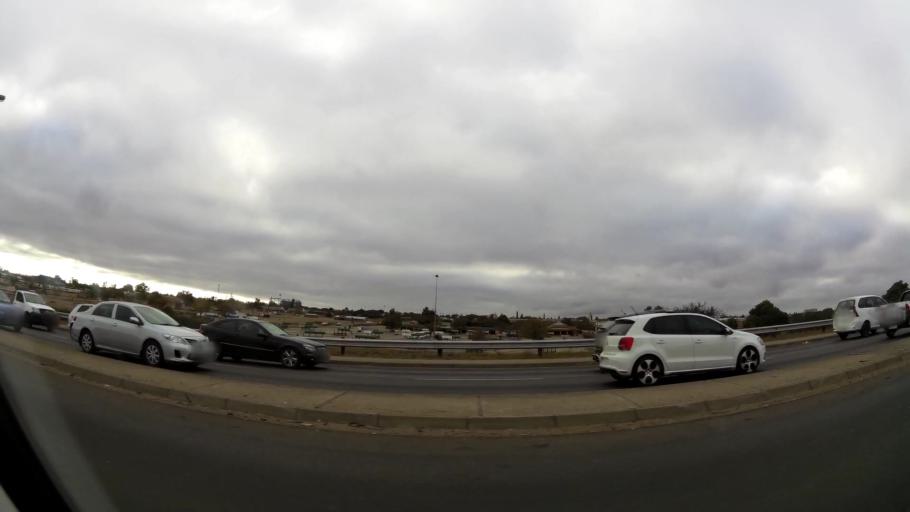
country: ZA
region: Limpopo
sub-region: Capricorn District Municipality
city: Polokwane
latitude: -23.9014
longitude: 29.4404
